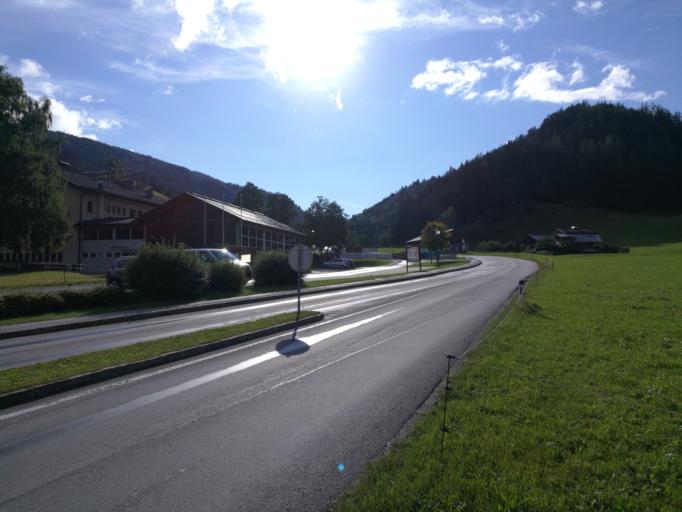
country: AT
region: Salzburg
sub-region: Politischer Bezirk Sankt Johann im Pongau
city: Forstau
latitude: 47.3789
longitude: 13.5513
